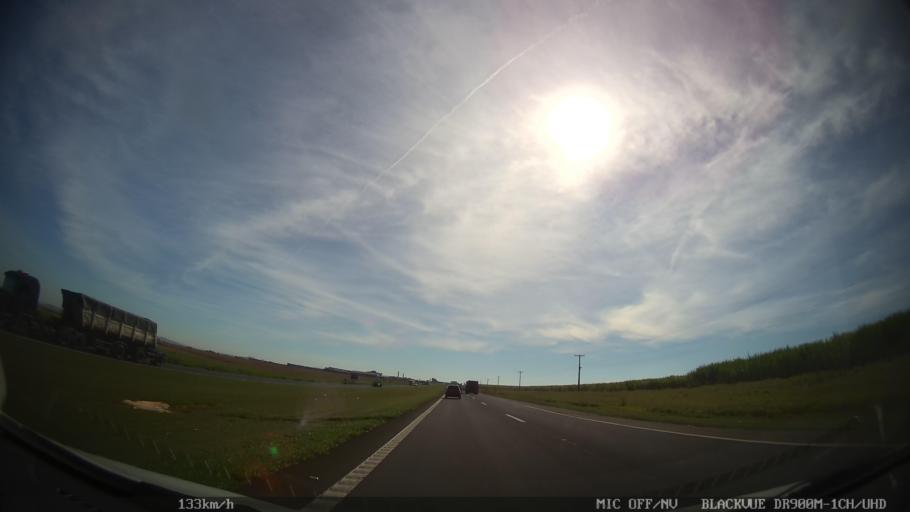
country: BR
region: Sao Paulo
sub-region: Araras
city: Araras
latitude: -22.4268
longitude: -47.3936
